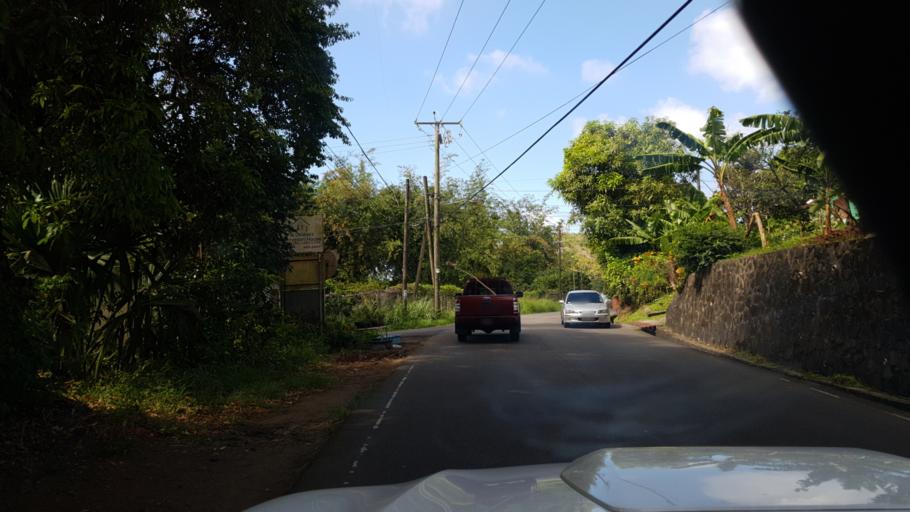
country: LC
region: Castries Quarter
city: Bisee
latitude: 14.0208
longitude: -60.9597
